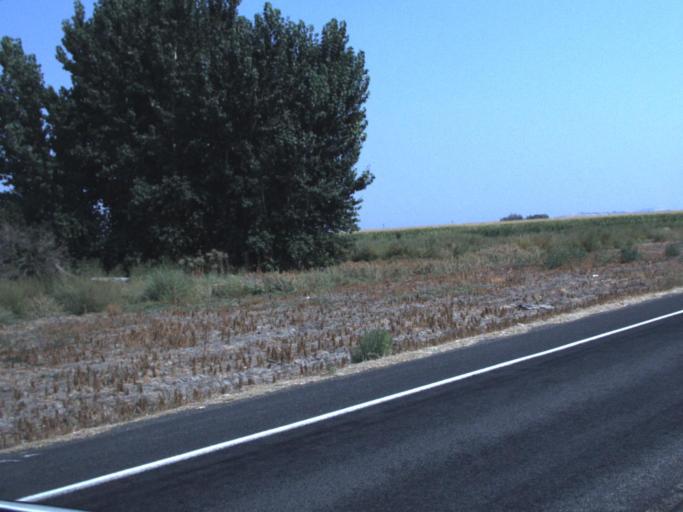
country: US
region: Washington
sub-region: Yakima County
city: Toppenish
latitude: 46.3527
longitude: -120.2853
